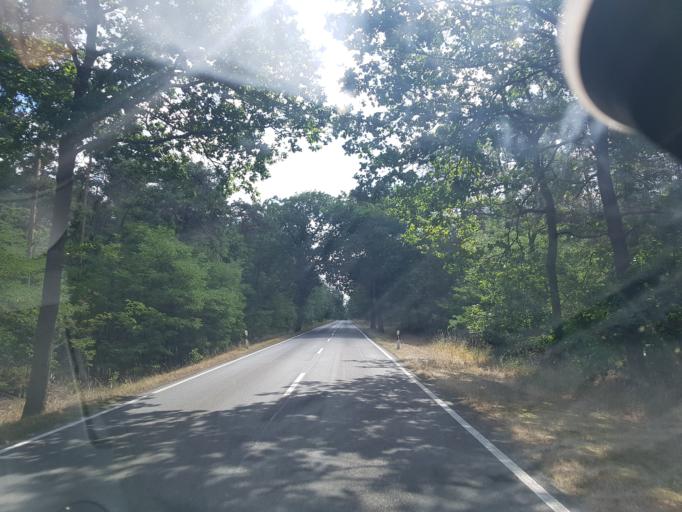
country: DE
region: Brandenburg
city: Drebkau
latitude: 51.6639
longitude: 14.1923
